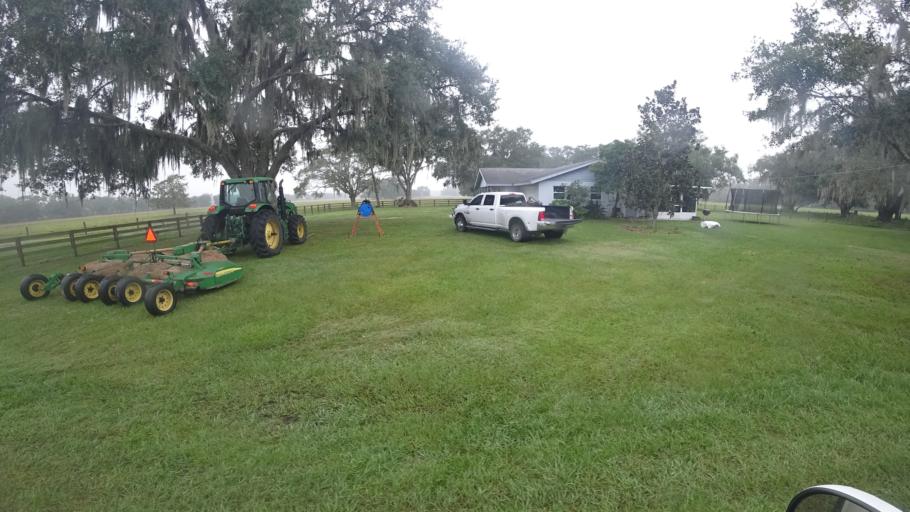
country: US
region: Florida
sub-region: Sarasota County
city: Lake Sarasota
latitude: 27.2920
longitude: -82.2348
